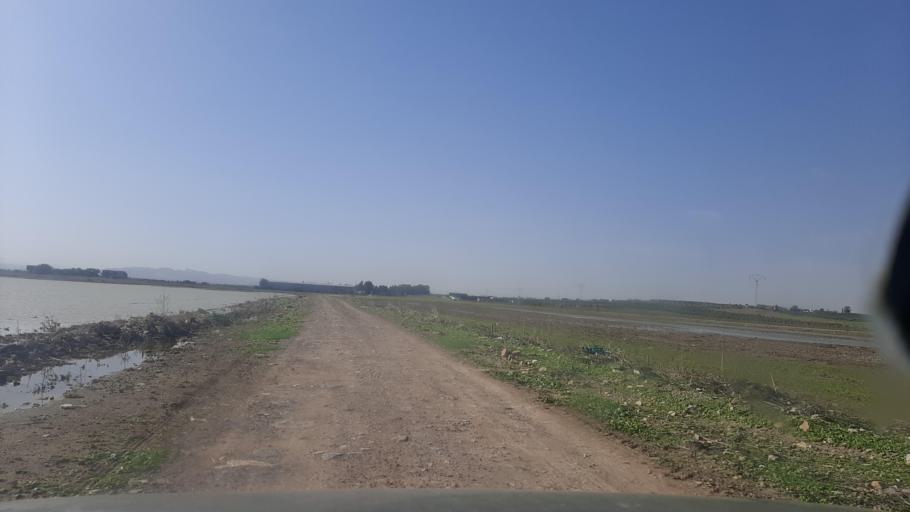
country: TN
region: Tunis
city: La Mohammedia
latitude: 36.6501
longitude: 10.0878
